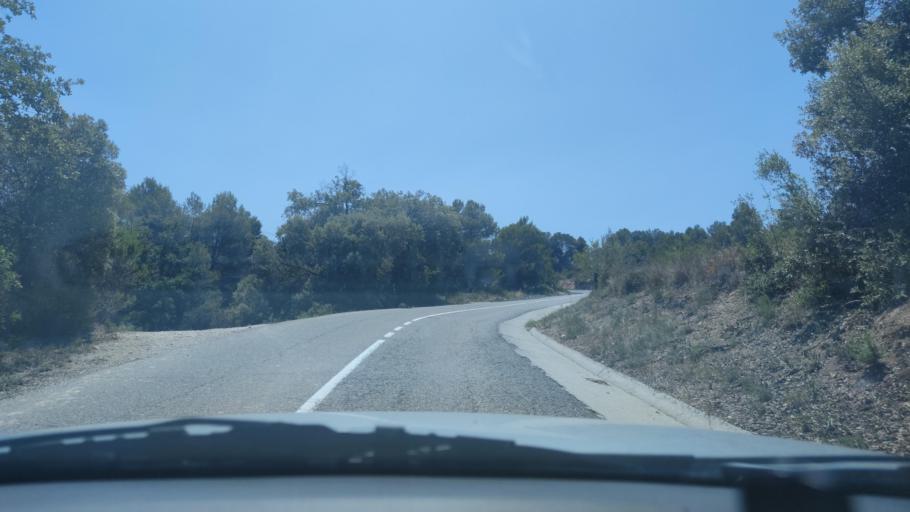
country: ES
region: Catalonia
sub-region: Provincia de Lleida
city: Vinaixa
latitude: 41.4096
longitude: 0.9578
